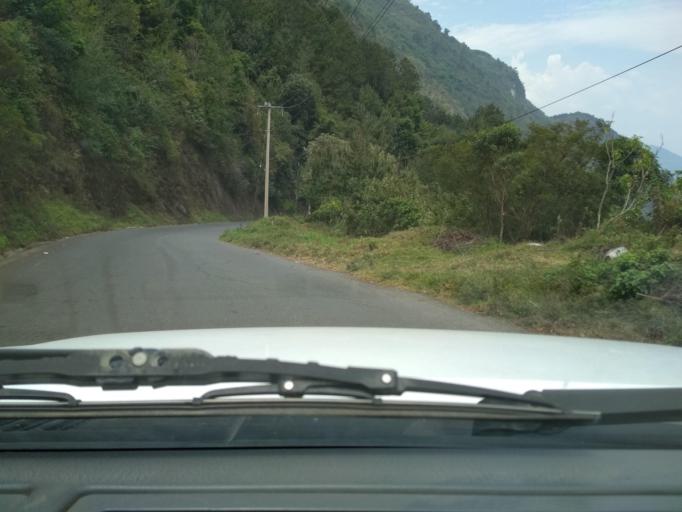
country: MX
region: Veracruz
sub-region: Camerino Z. Mendoza
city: La Cuesta
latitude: 18.7862
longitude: -97.1596
